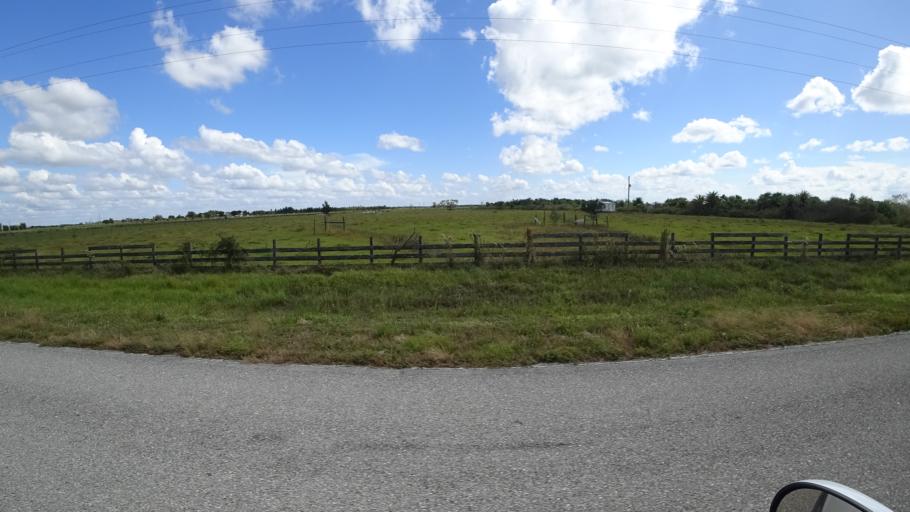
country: US
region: Florida
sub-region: Sarasota County
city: Warm Mineral Springs
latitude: 27.2895
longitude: -82.1918
